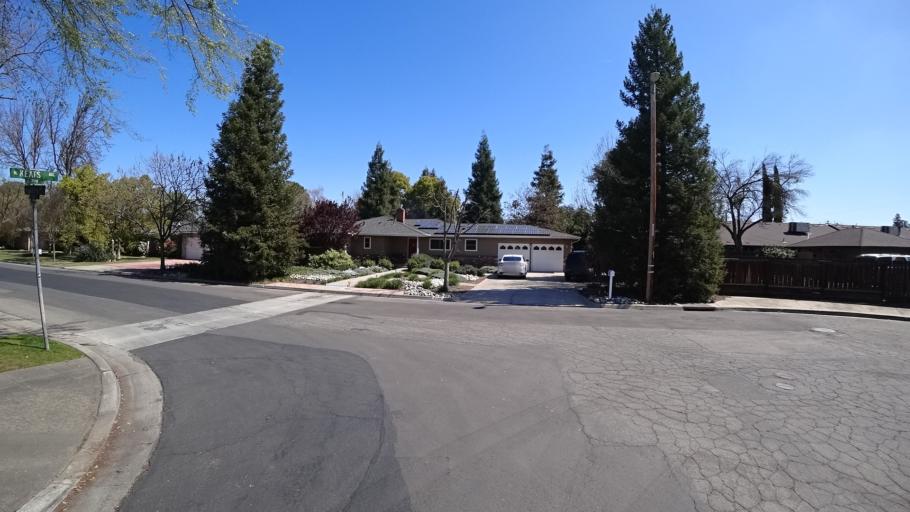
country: US
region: California
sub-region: Fresno County
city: Fresno
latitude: 36.8104
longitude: -119.7962
